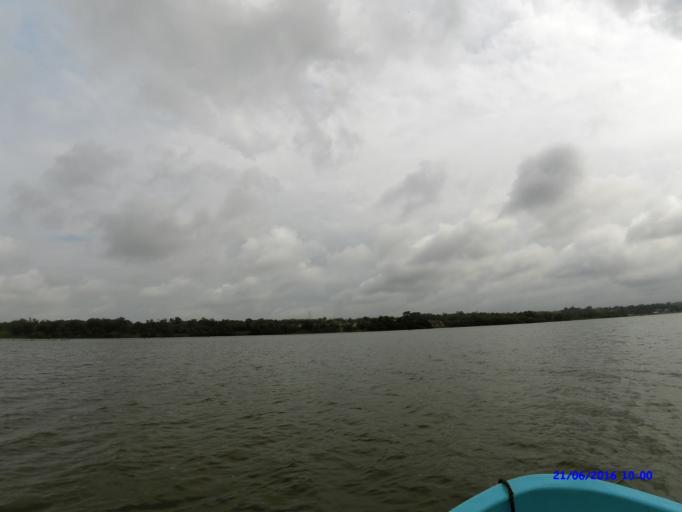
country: BJ
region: Mono
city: Come
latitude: 6.4493
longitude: 1.9263
